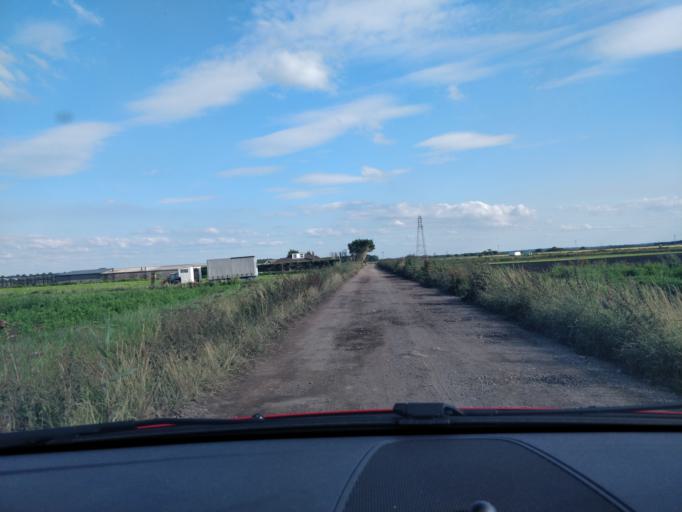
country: GB
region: England
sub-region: Lancashire
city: Banks
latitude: 53.6635
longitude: -2.9183
